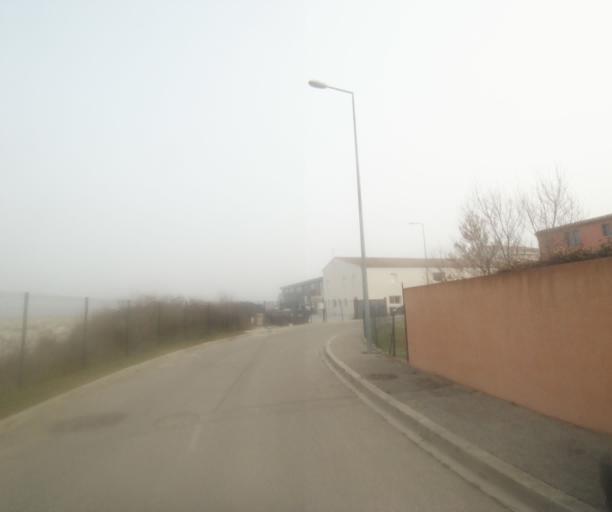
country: FR
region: Provence-Alpes-Cote d'Azur
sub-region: Departement des Bouches-du-Rhone
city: Eguilles
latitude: 43.5467
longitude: 5.3573
